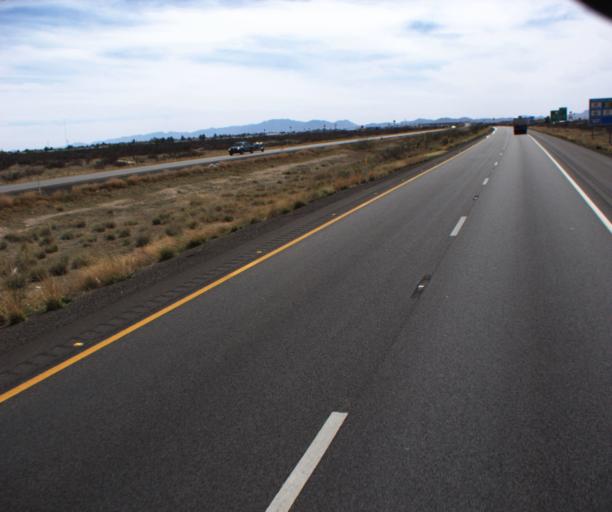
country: US
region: Arizona
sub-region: Cochise County
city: Willcox
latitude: 32.2786
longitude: -109.8331
